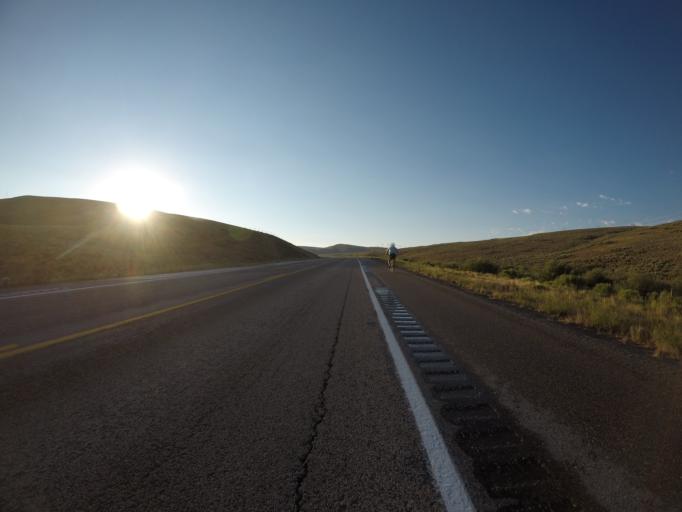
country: US
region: Wyoming
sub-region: Lincoln County
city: Kemmerer
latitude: 41.8702
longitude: -110.5102
